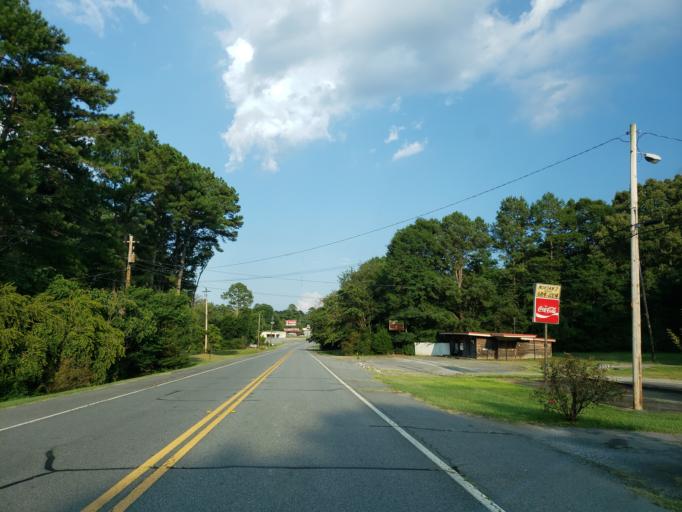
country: US
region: Georgia
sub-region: Polk County
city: Rockmart
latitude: 34.0062
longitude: -85.0681
